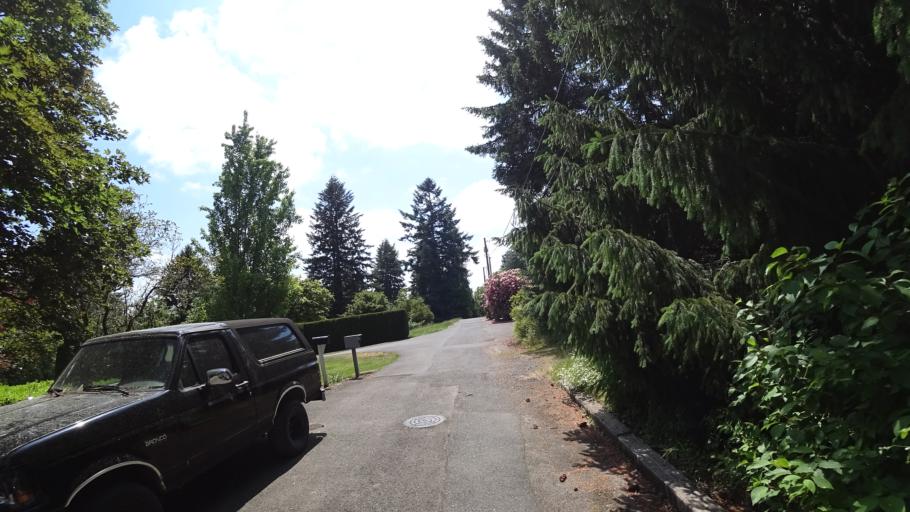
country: US
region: Oregon
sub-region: Clackamas County
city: Lake Oswego
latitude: 45.4373
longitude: -122.7026
